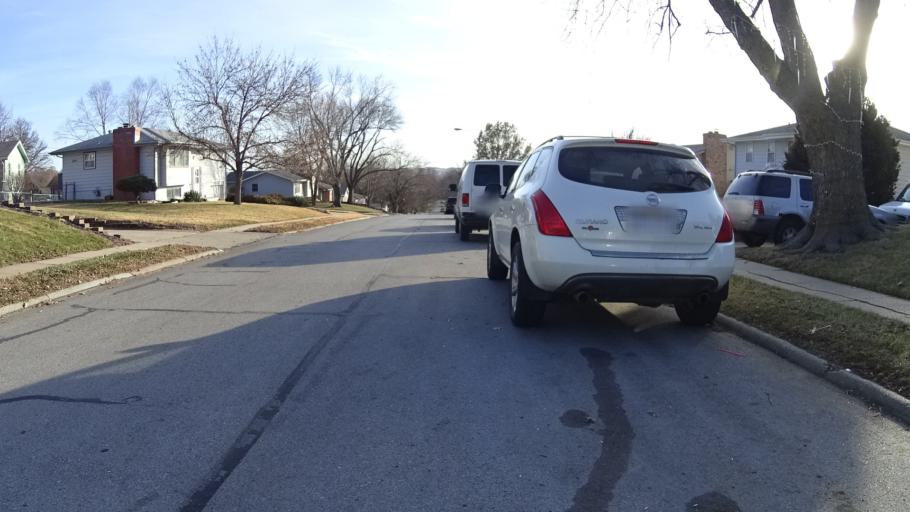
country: US
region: Nebraska
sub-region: Sarpy County
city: La Vista
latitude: 41.1882
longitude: -95.9969
